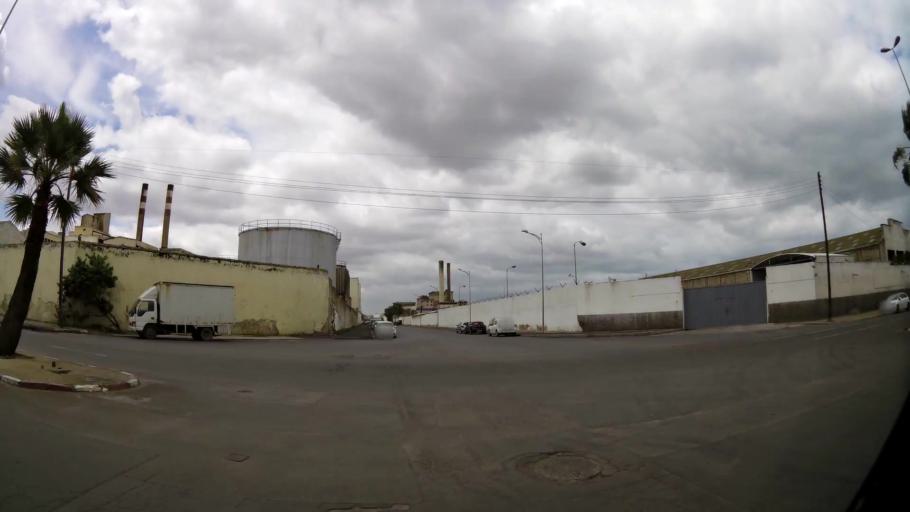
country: MA
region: Grand Casablanca
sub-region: Casablanca
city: Casablanca
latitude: 33.6085
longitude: -7.5644
